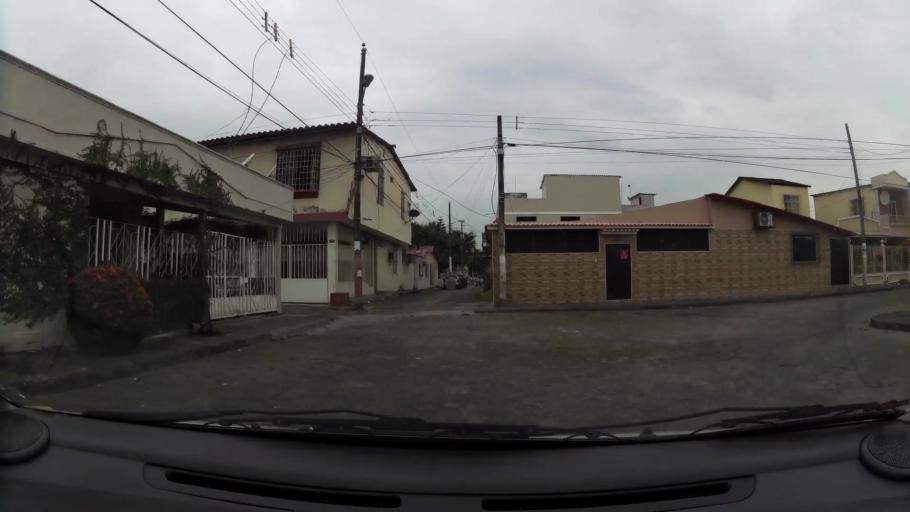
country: EC
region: Guayas
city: Eloy Alfaro
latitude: -2.1370
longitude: -79.9021
